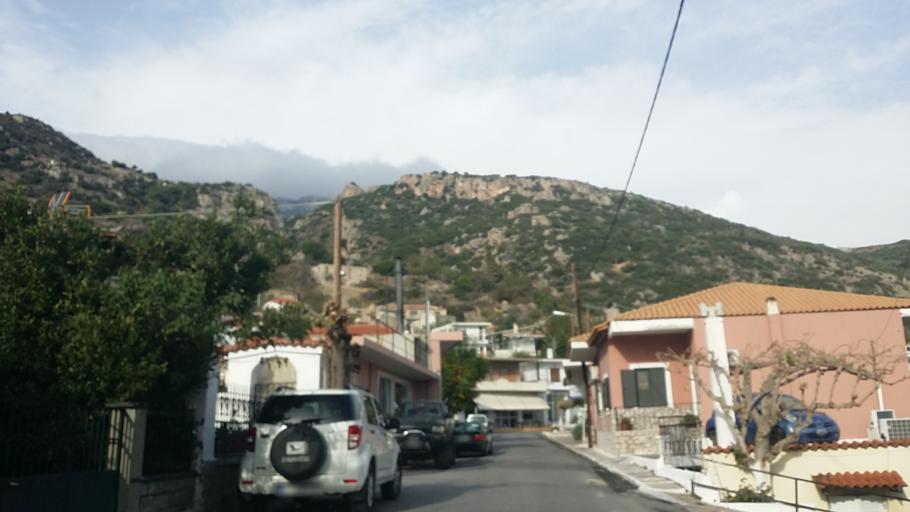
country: GR
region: Central Greece
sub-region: Nomos Voiotias
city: Korini
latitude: 38.2590
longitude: 22.9099
